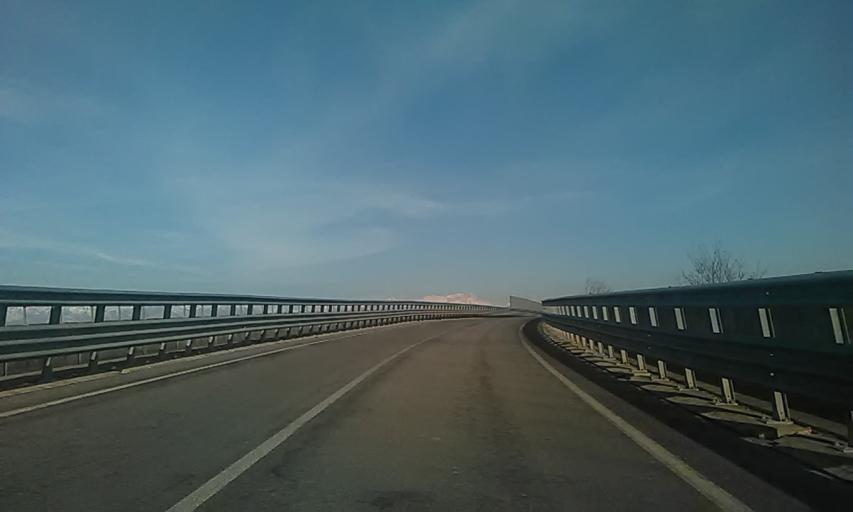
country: IT
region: Piedmont
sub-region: Provincia di Vercelli
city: Balocco
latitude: 45.4454
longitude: 8.2868
